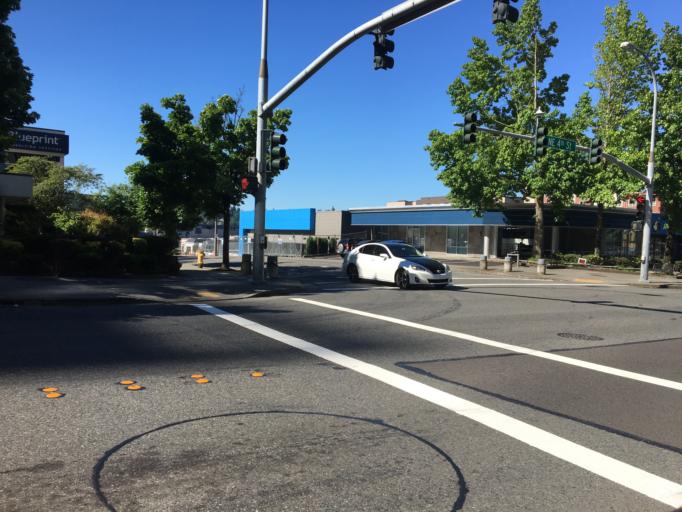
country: US
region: Washington
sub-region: King County
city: Bellevue
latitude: 47.6138
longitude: -122.1986
